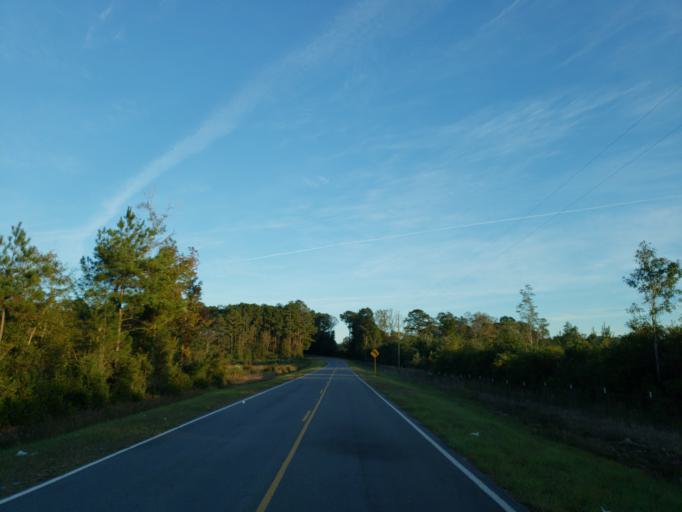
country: US
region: Mississippi
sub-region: Wayne County
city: Belmont
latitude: 31.4426
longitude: -88.5113
